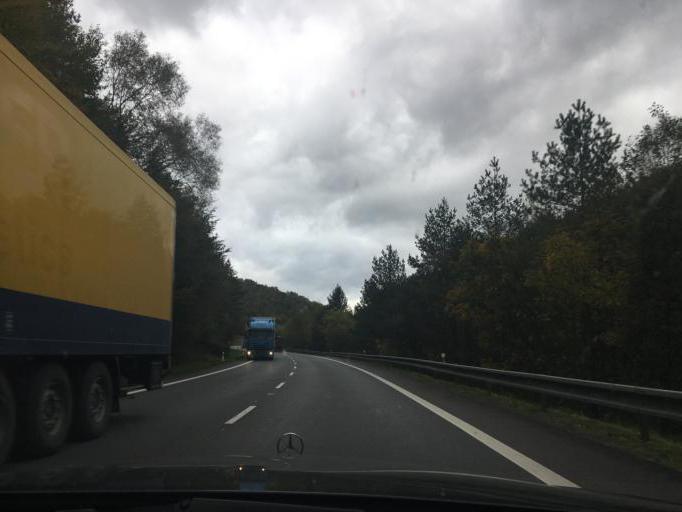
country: PL
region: Subcarpathian Voivodeship
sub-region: Powiat krosnienski
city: Jasliska
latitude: 49.3903
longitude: 21.6993
